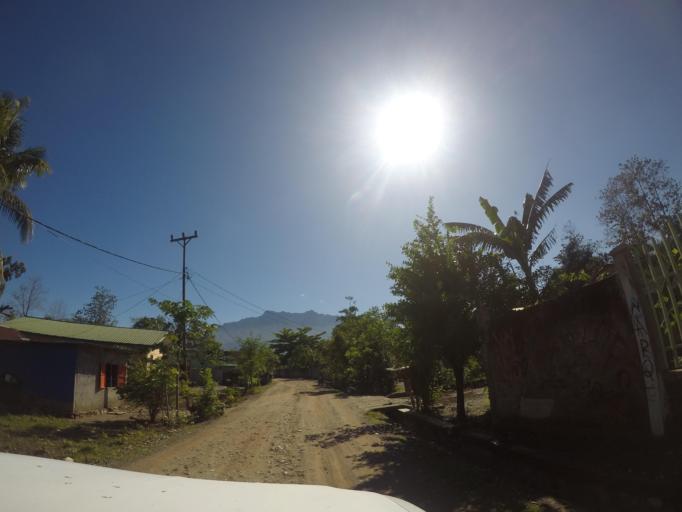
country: TL
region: Bobonaro
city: Maliana
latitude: -8.9918
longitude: 125.2120
